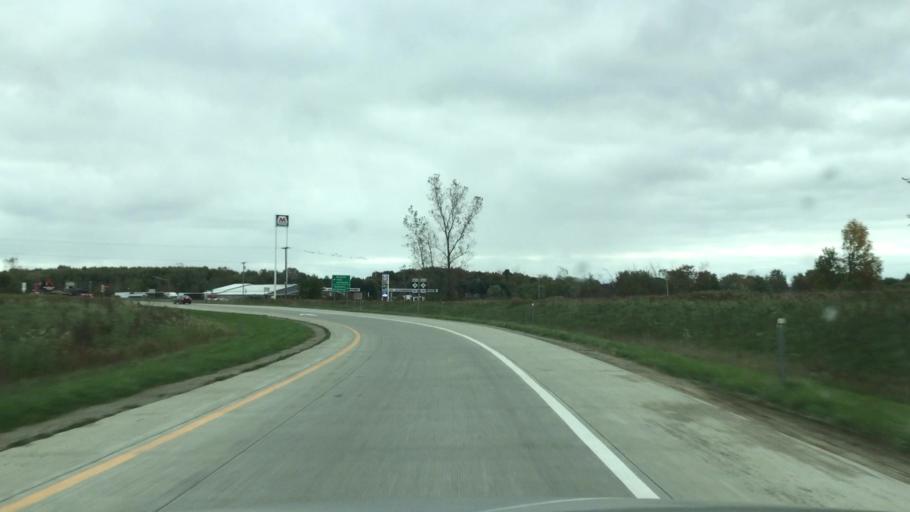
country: US
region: Michigan
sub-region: Macomb County
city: Memphis
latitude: 42.9781
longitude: -82.7674
